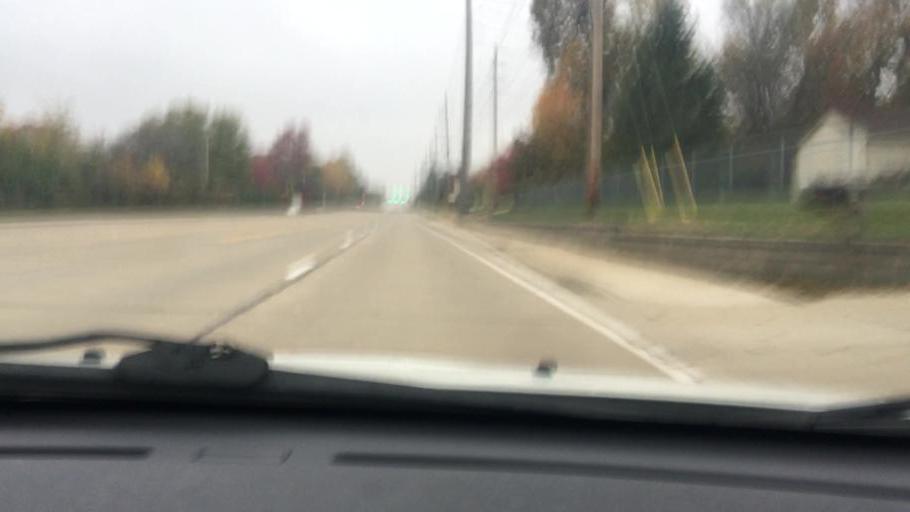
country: US
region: Missouri
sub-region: Saint Charles County
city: O'Fallon
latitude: 38.8218
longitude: -90.6859
